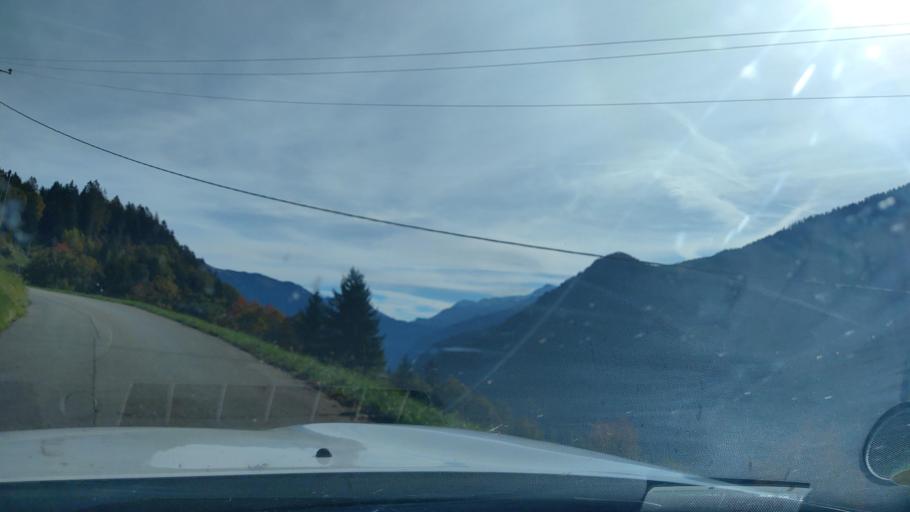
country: FR
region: Rhone-Alpes
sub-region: Departement de la Savoie
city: Beaufort
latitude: 45.7263
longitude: 6.4991
